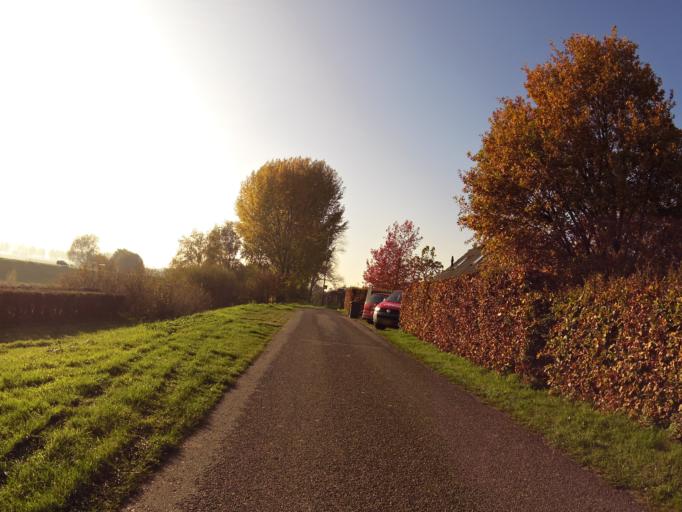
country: NL
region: Gelderland
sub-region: Gemeente Maasdriel
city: Hedel
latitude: 51.7337
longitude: 5.2714
